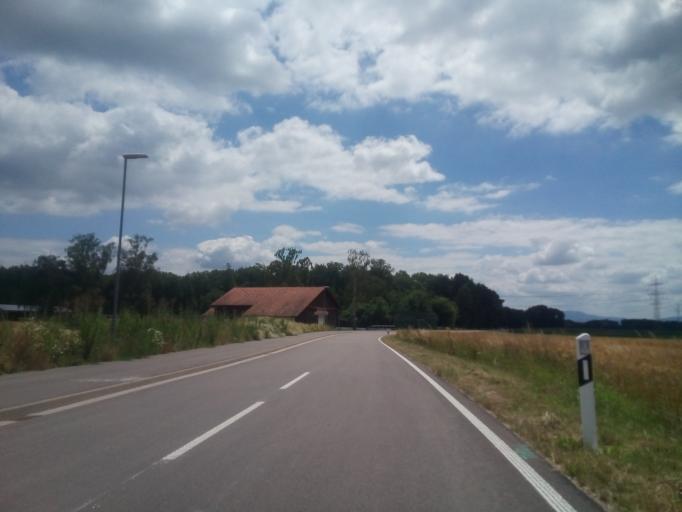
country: DE
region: Baden-Wuerttemberg
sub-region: Freiburg Region
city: Rheinau
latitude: 48.6496
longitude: 7.9350
